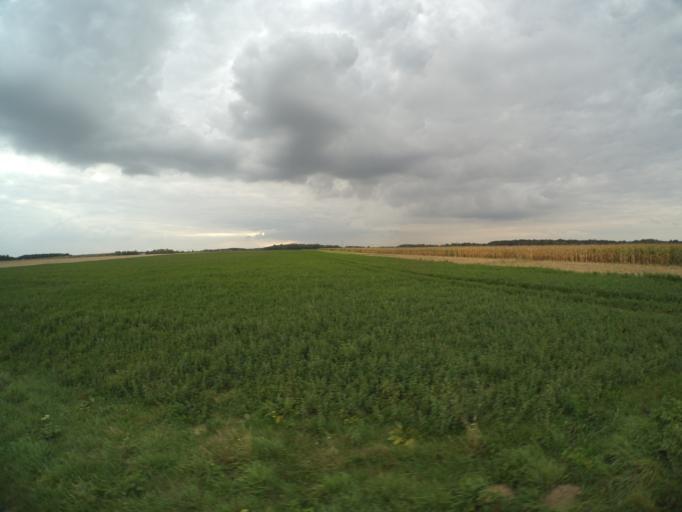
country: FR
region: Centre
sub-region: Departement d'Indre-et-Loire
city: Auzouer-en-Touraine
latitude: 47.4972
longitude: 0.9475
